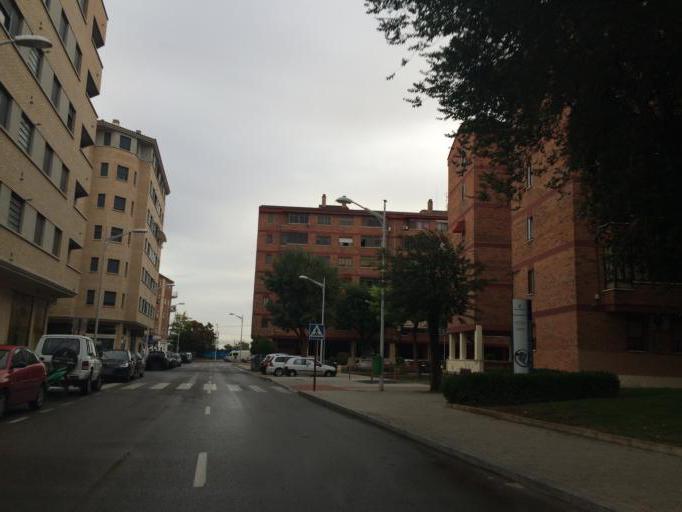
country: ES
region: Castille-La Mancha
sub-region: Provincia de Albacete
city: Albacete
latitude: 39.0001
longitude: -1.8525
